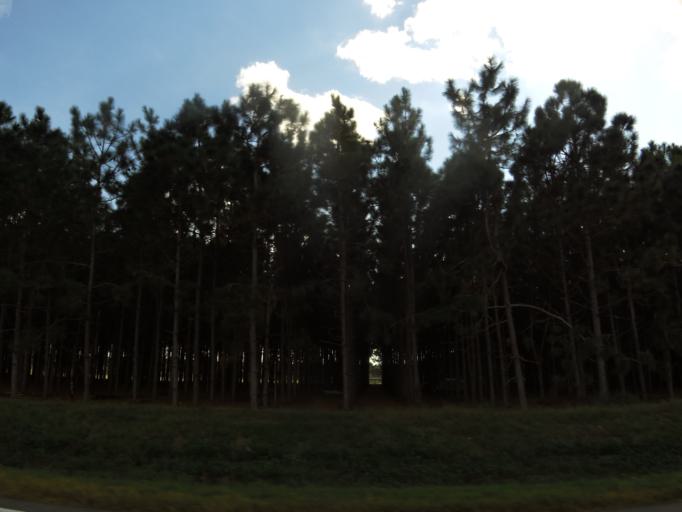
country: US
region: Georgia
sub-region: Lowndes County
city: Valdosta
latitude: 30.8104
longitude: -83.2279
